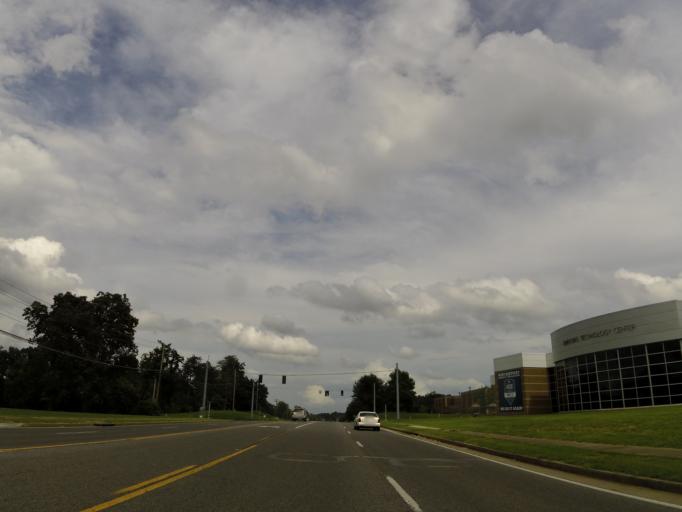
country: US
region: Kentucky
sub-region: McCracken County
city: Hendron
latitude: 37.0535
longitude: -88.6683
